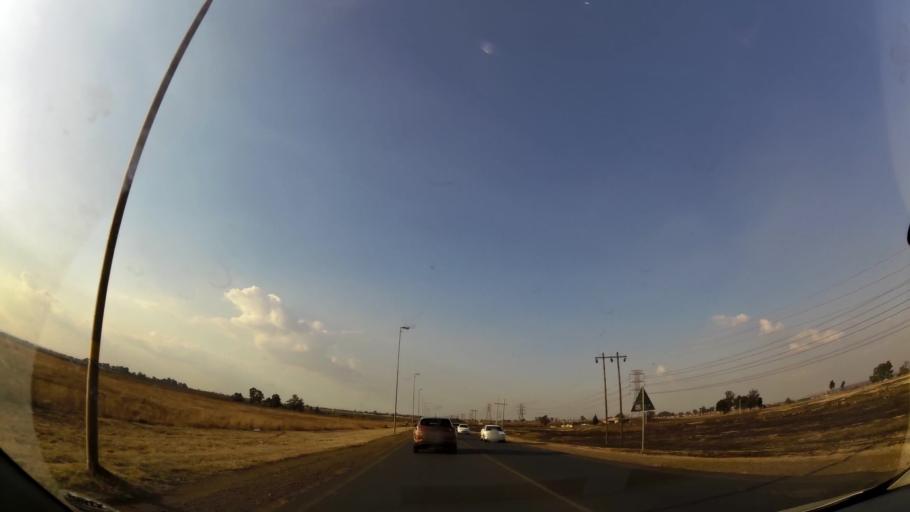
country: ZA
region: Gauteng
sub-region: Ekurhuleni Metropolitan Municipality
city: Germiston
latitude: -26.3323
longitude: 28.2339
